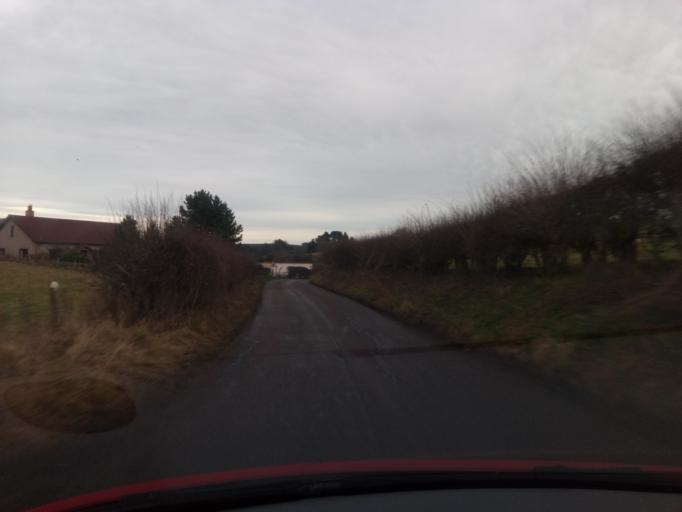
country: GB
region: England
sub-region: Northumberland
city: Wooler
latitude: 55.5513
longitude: -2.0298
